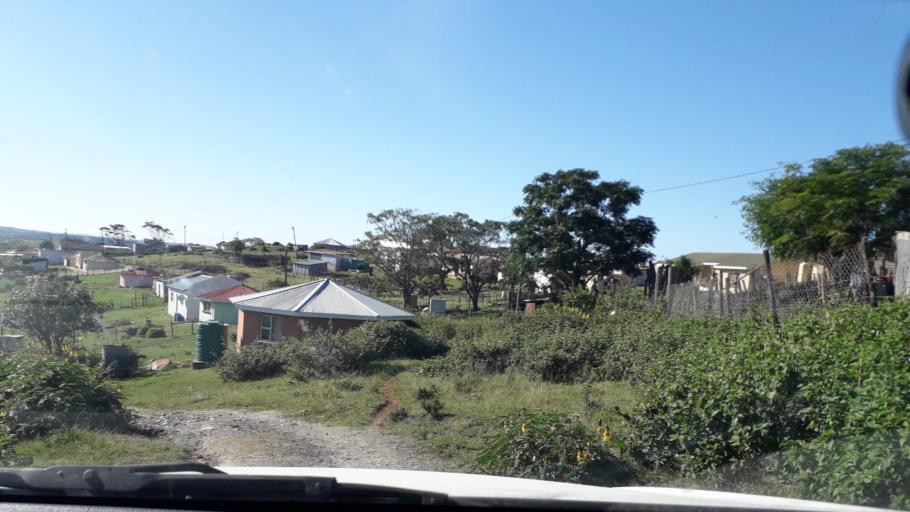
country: ZA
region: Eastern Cape
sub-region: Buffalo City Metropolitan Municipality
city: East London
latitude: -32.8424
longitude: 27.9877
